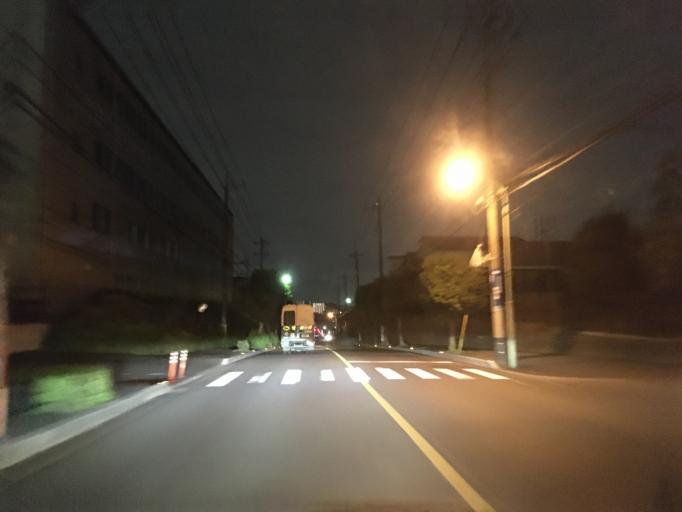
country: JP
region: Saitama
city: Sayama
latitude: 35.8690
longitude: 139.3960
